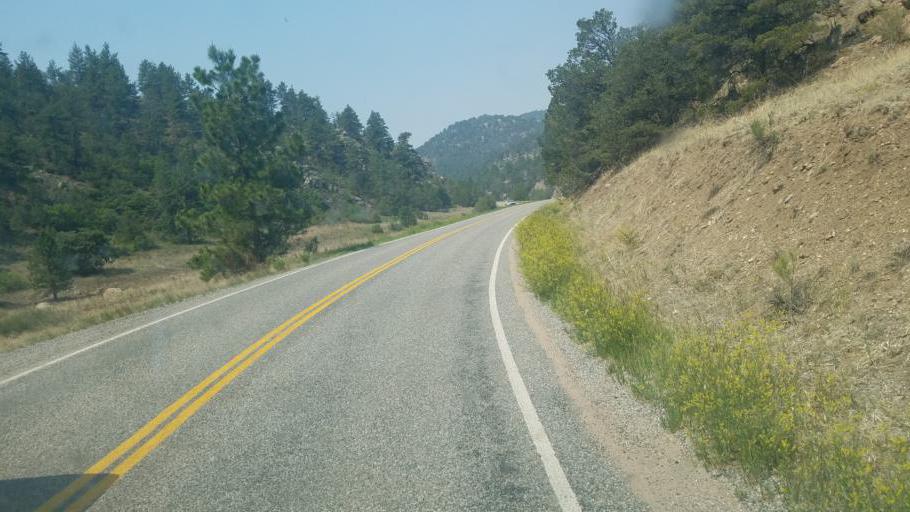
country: US
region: Colorado
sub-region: Fremont County
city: Canon City
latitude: 38.3897
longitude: -105.4522
